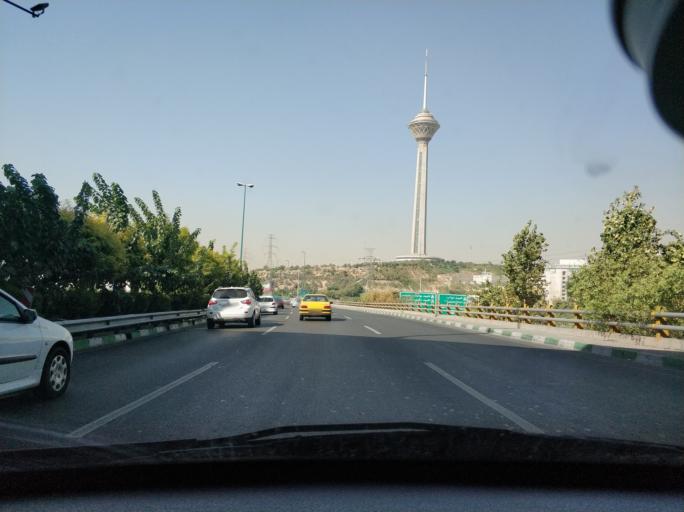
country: IR
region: Tehran
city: Tehran
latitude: 35.7436
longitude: 51.3870
